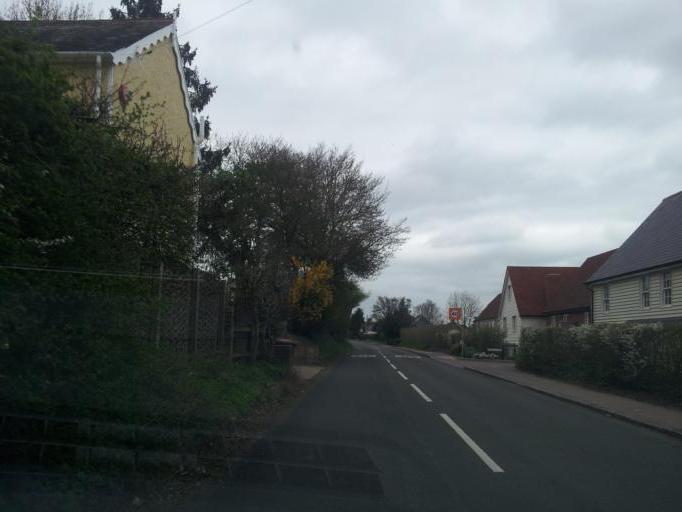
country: GB
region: England
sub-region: Hertfordshire
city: Buntingford
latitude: 51.9096
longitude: 0.0247
